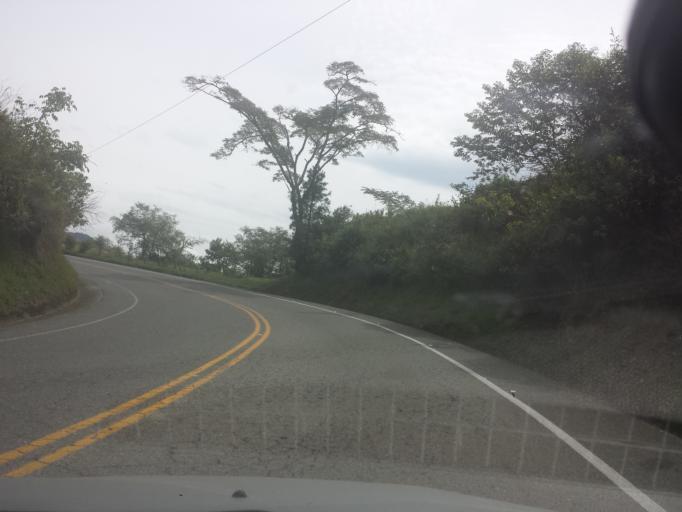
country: CO
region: Antioquia
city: Liborina
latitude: 6.6384
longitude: -75.8714
